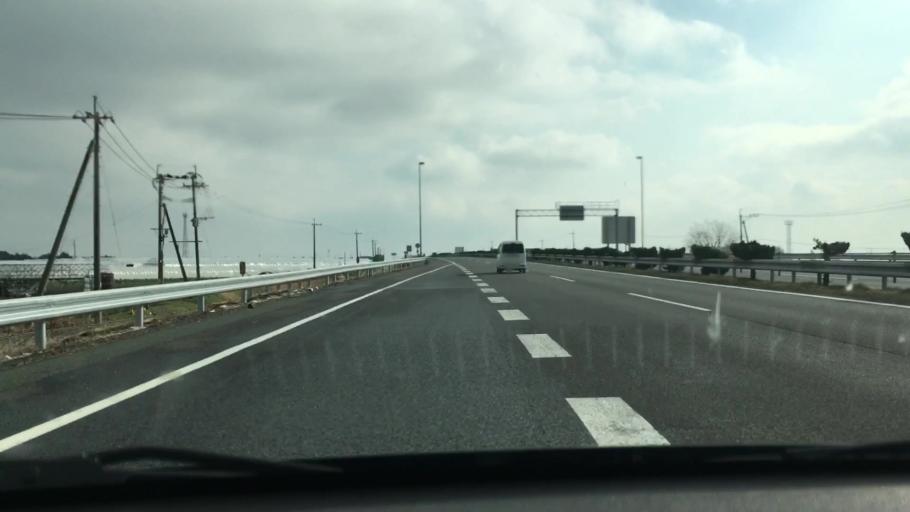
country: JP
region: Kumamoto
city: Ueki
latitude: 32.8922
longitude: 130.7204
